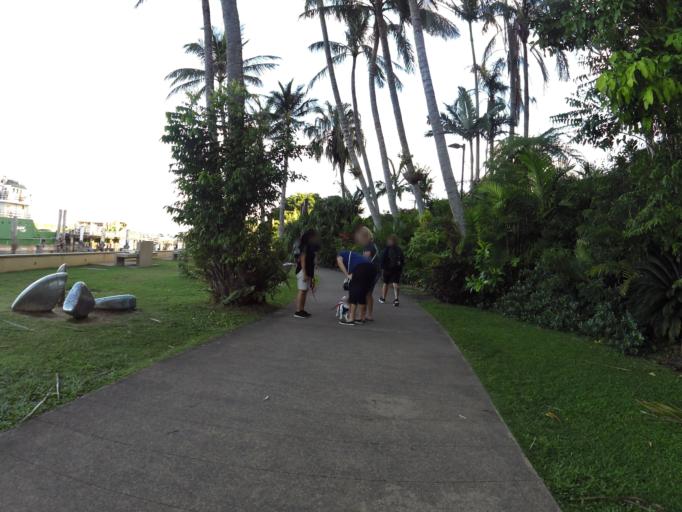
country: AU
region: Queensland
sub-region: Cairns
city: Cairns
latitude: -16.9230
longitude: 145.7807
